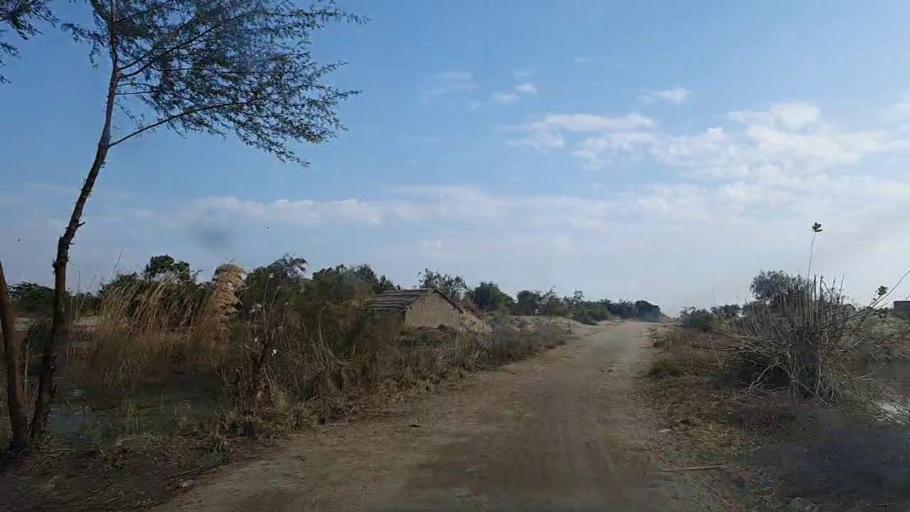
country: PK
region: Sindh
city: Sanghar
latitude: 26.2038
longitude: 69.0256
